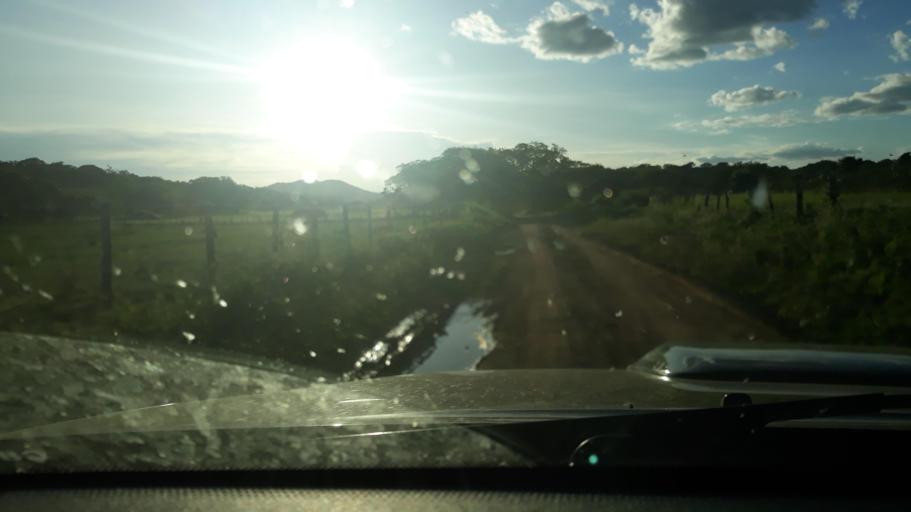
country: BR
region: Bahia
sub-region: Riacho De Santana
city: Riacho de Santana
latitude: -13.8457
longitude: -42.7564
